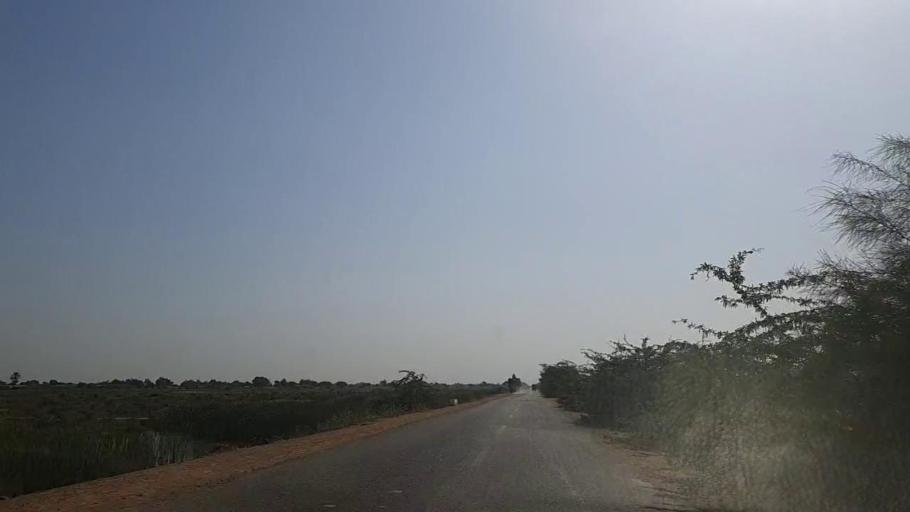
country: PK
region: Sindh
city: Mirpur Batoro
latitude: 24.5826
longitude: 68.2898
